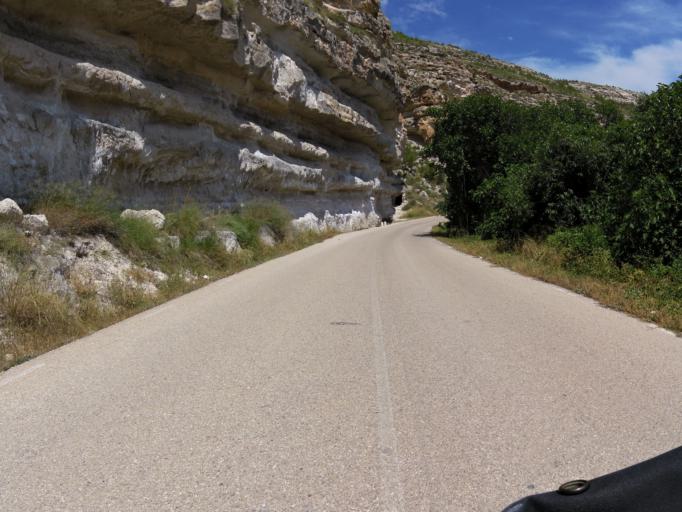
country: ES
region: Castille-La Mancha
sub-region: Provincia de Albacete
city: Jorquera
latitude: 39.1720
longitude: -1.5418
